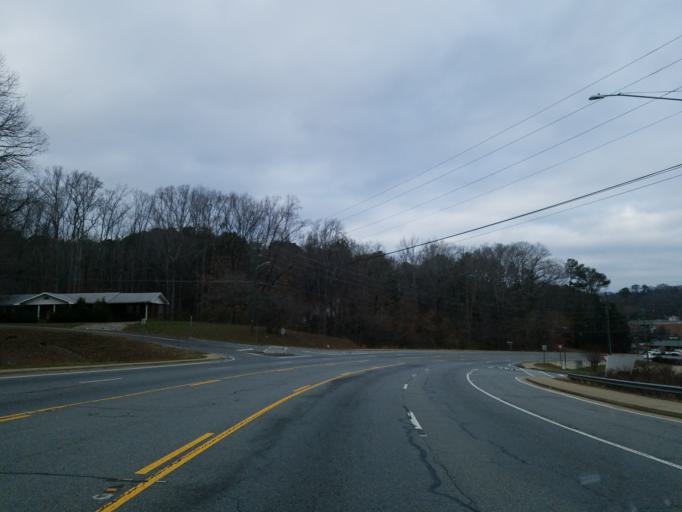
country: US
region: Georgia
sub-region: Cherokee County
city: Canton
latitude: 34.2413
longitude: -84.4980
